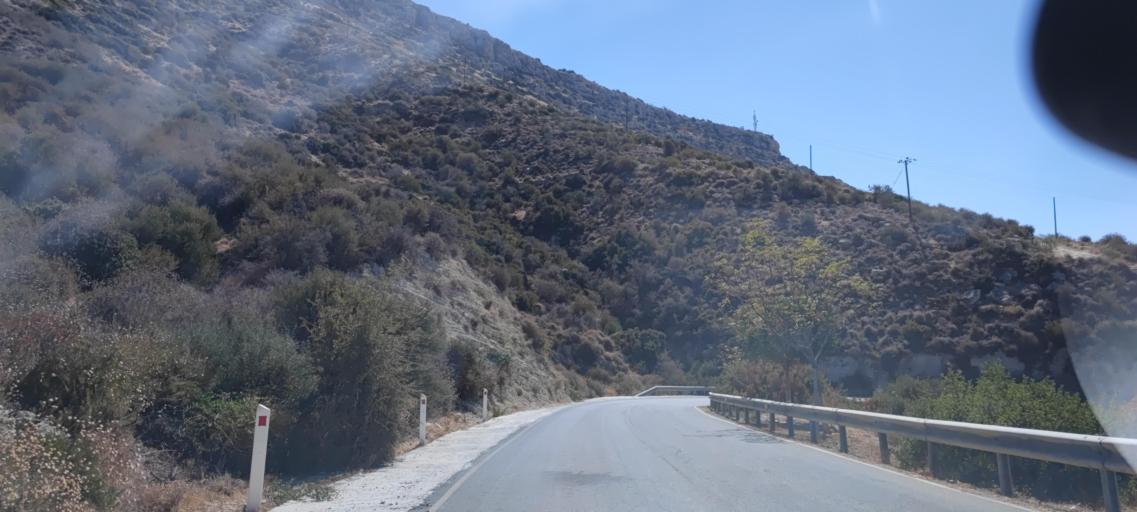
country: CY
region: Limassol
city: Mouttagiaka
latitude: 34.7432
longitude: 33.0873
